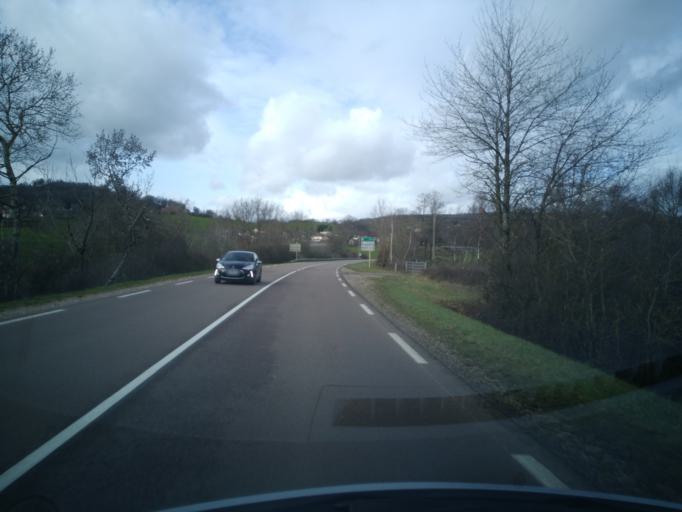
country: FR
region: Bourgogne
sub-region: Departement de Saone-et-Loire
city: Montcenis
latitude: 46.7854
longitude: 4.4055
